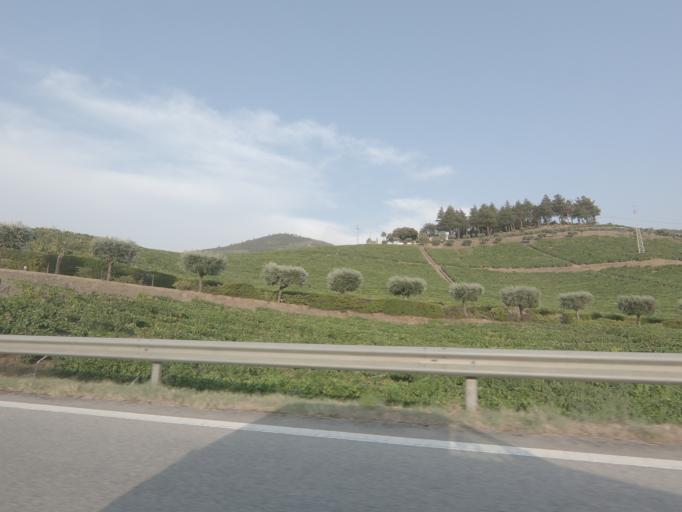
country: PT
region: Viseu
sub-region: Armamar
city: Armamar
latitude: 41.1470
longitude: -7.6867
